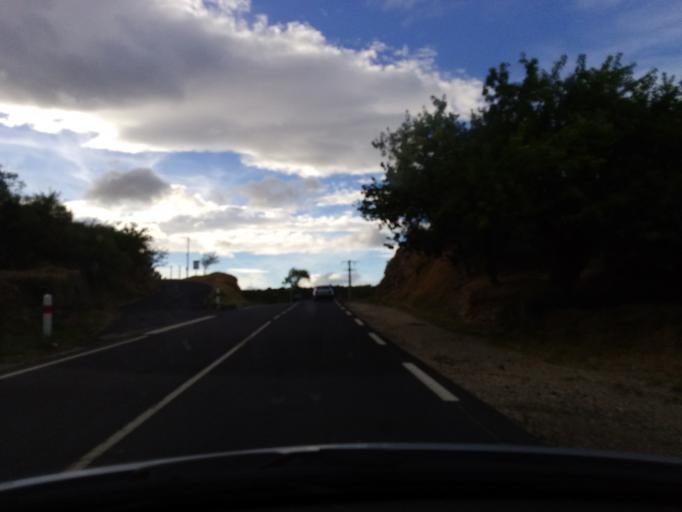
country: FR
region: Languedoc-Roussillon
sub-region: Departement de l'Herault
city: Nebian
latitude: 43.6401
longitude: 3.4179
